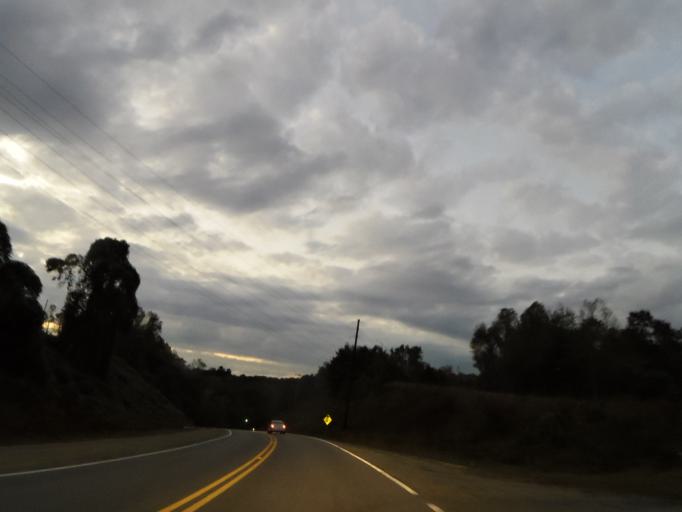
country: US
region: North Carolina
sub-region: Madison County
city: Marshall
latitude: 35.8515
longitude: -82.7344
